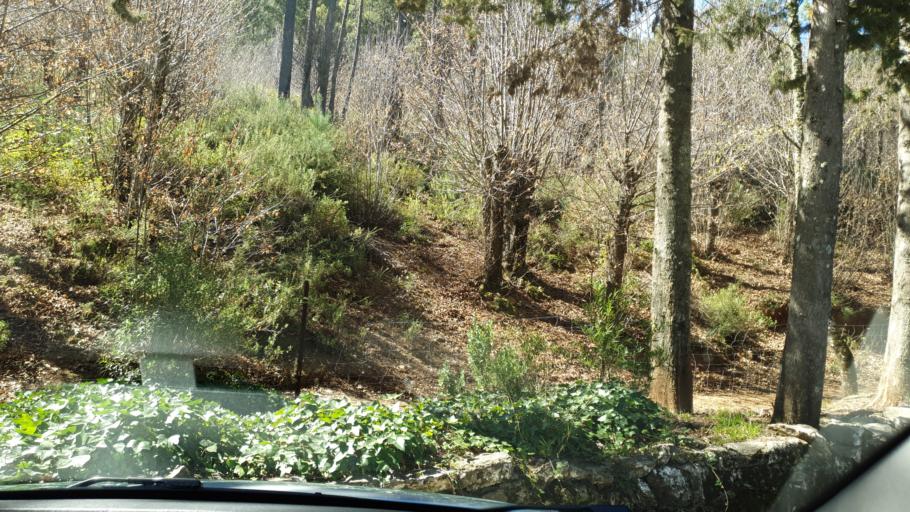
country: ES
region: Andalusia
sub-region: Provincia de Malaga
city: Ojen
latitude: 36.5799
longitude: -4.8855
